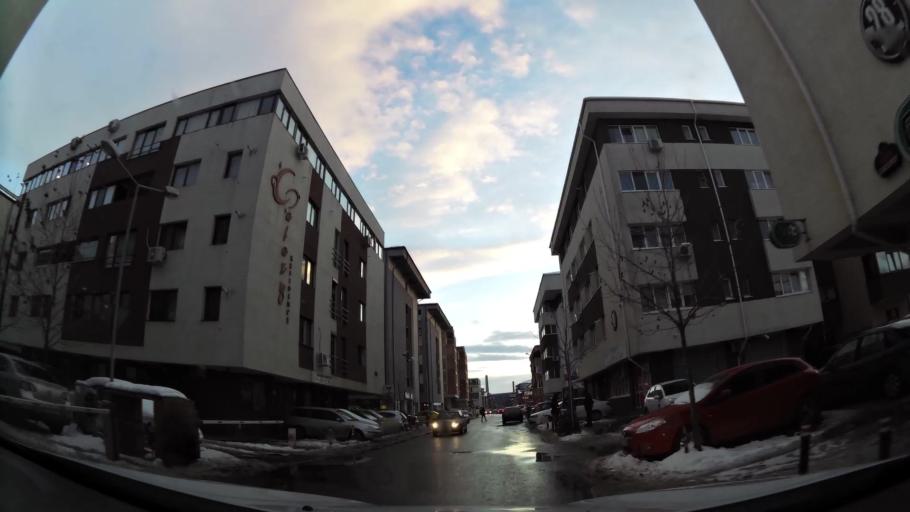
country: RO
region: Ilfov
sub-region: Comuna Popesti-Leordeni
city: Popesti-Leordeni
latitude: 44.3739
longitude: 26.1504
